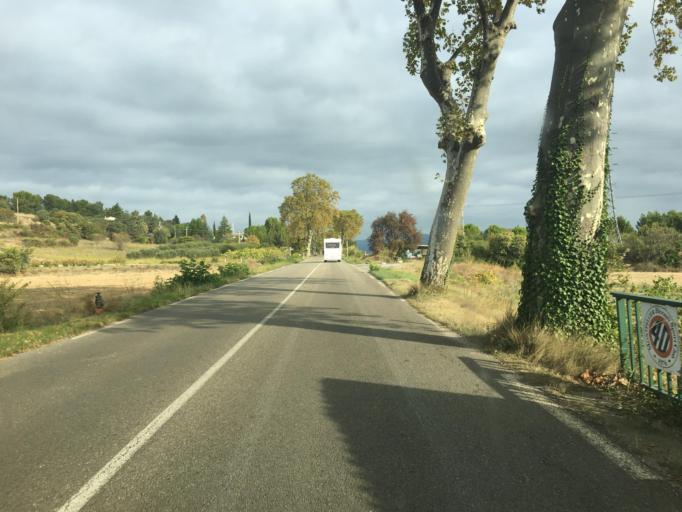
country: FR
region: Languedoc-Roussillon
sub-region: Departement de l'Herault
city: Nebian
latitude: 43.6116
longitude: 3.4369
